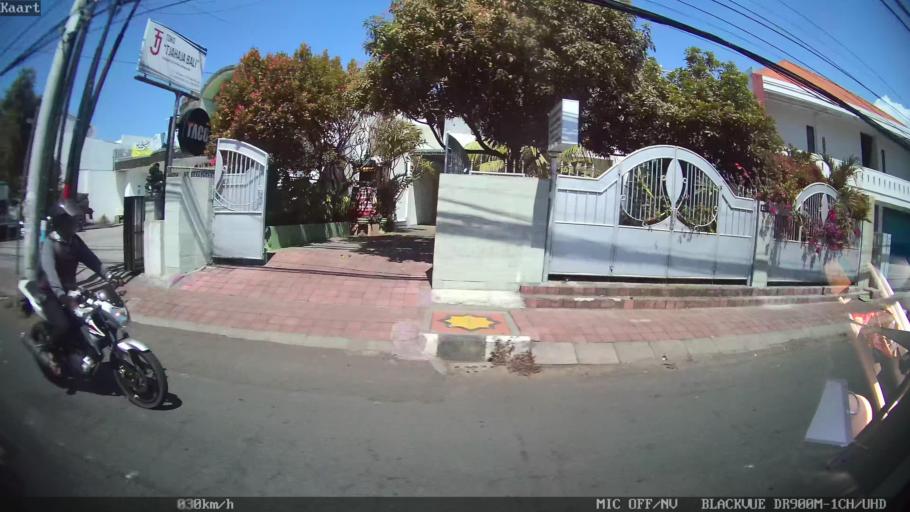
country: ID
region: Bali
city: Banjar Galiran
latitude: -8.1217
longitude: 115.0716
